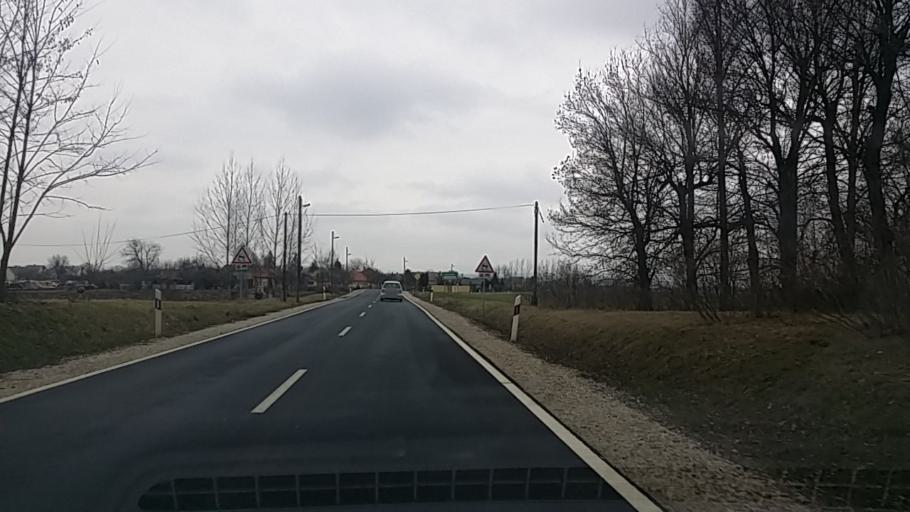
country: HU
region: Borsod-Abauj-Zemplen
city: Sajoszentpeter
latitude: 48.2399
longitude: 20.7282
